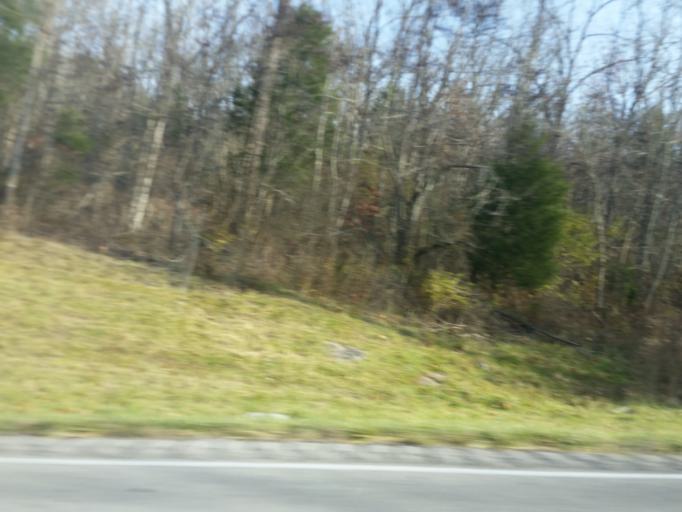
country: US
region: Kentucky
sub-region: Harrison County
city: Cynthiana
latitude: 38.4869
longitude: -84.2842
